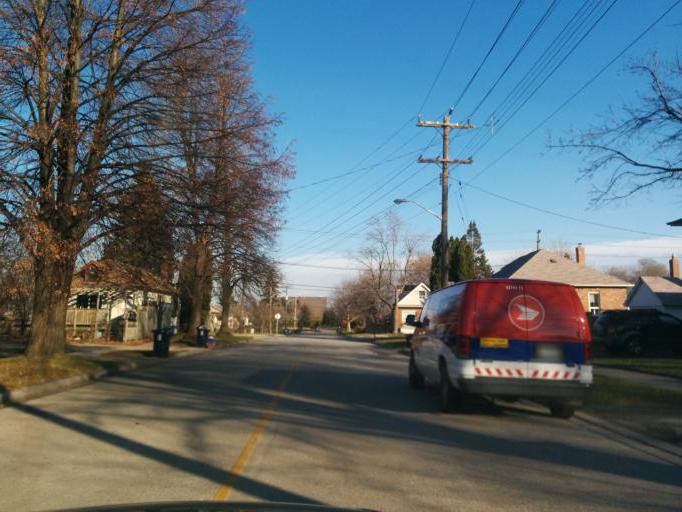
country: CA
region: Ontario
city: Etobicoke
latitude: 43.6094
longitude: -79.5322
